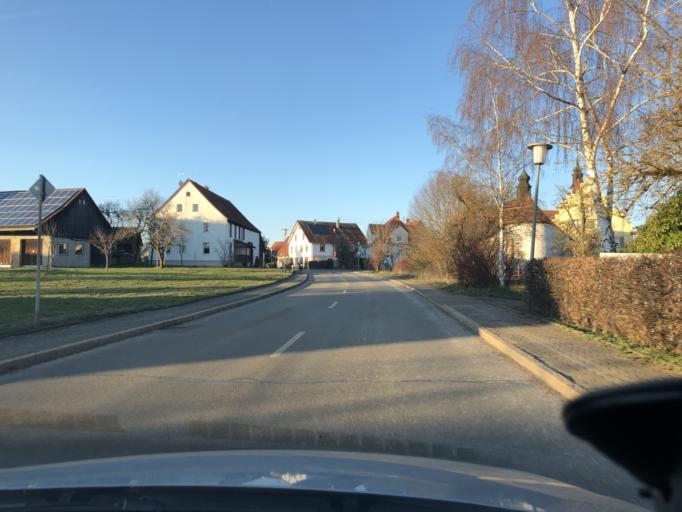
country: DE
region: Baden-Wuerttemberg
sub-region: Freiburg Region
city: Hufingen
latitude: 47.8680
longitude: 8.4646
